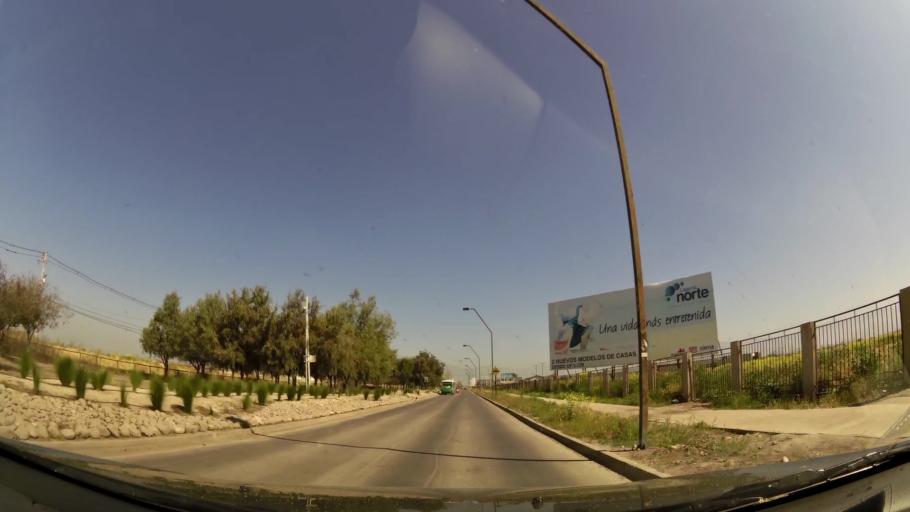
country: CL
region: Santiago Metropolitan
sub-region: Provincia de Chacabuco
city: Chicureo Abajo
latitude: -33.3280
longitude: -70.7590
